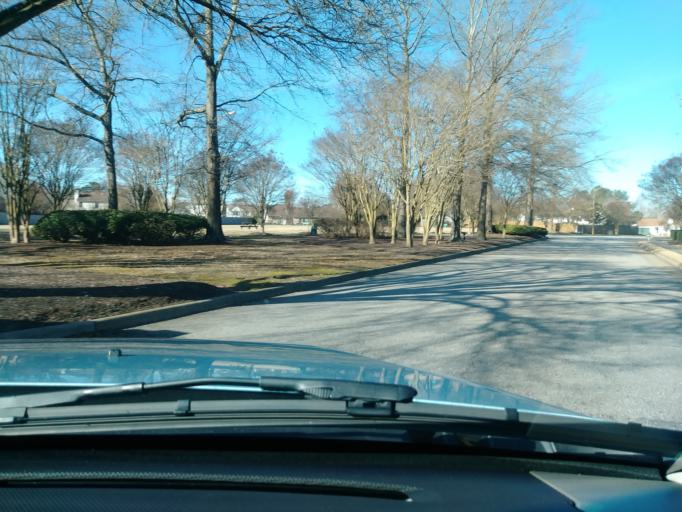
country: US
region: Virginia
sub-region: City of Chesapeake
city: Chesapeake
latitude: 36.7546
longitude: -76.2071
